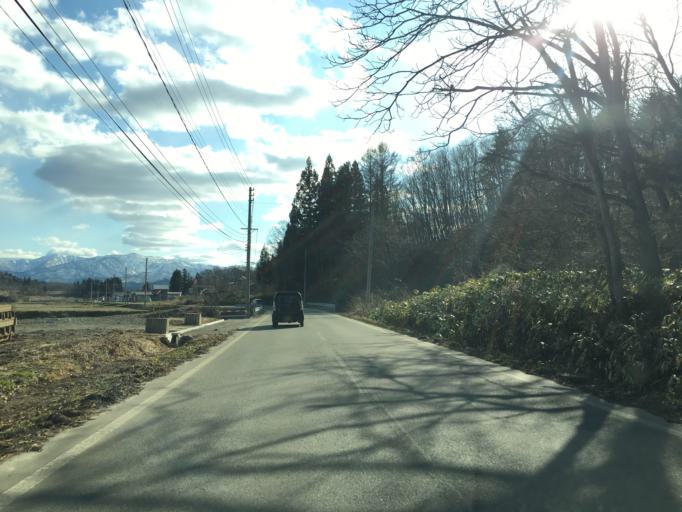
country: JP
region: Yamagata
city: Nagai
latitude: 37.9780
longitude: 139.9993
